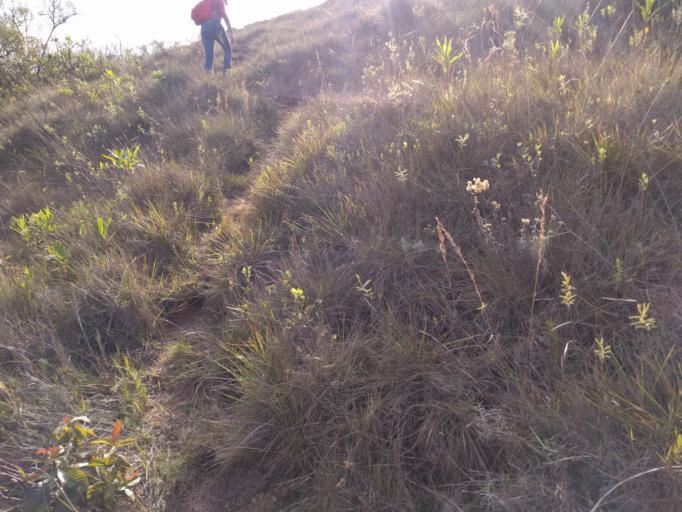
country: BO
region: Santa Cruz
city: Samaipata
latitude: -18.1853
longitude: -63.8899
